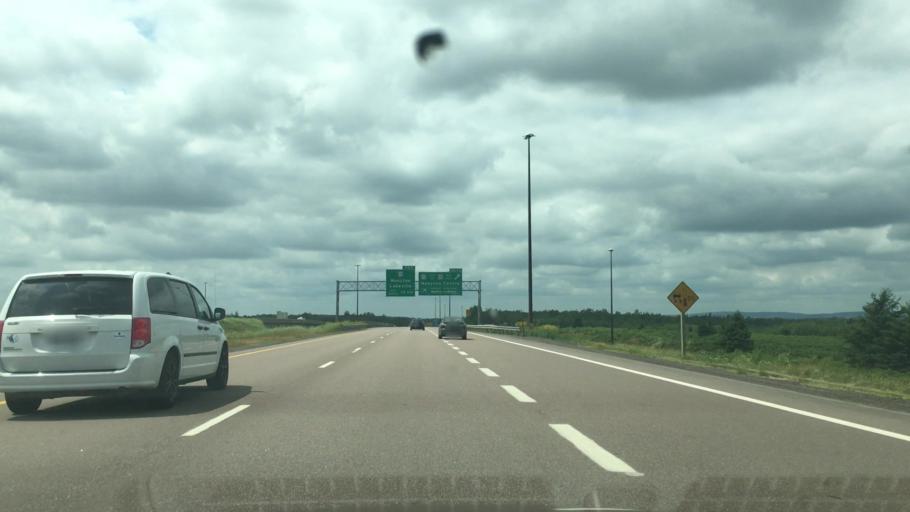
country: CA
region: New Brunswick
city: Dieppe
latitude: 46.1287
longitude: -64.6773
